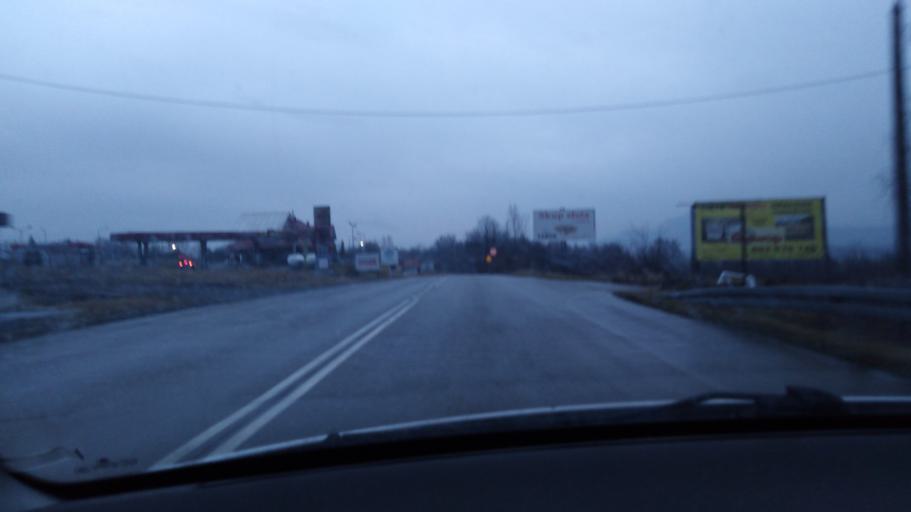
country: PL
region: Silesian Voivodeship
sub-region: Powiat zywiecki
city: Radziechowy
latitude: 49.6308
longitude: 19.1514
